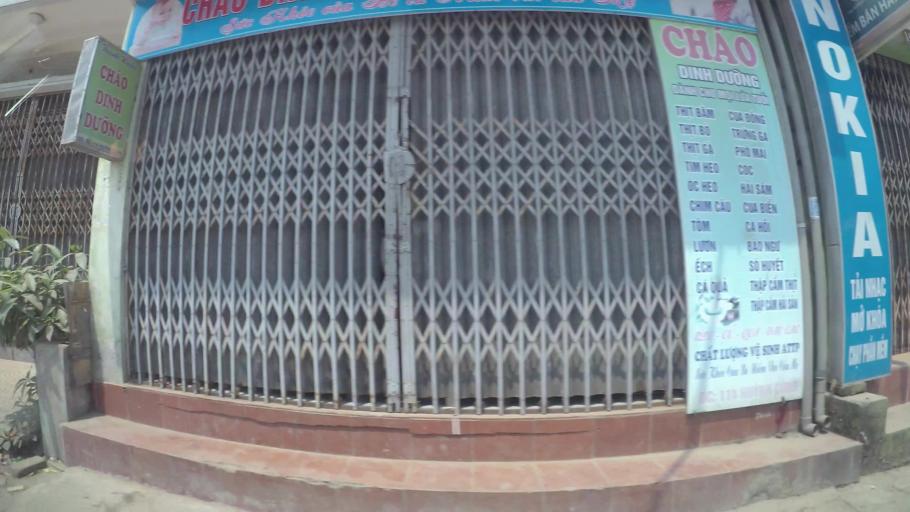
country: VN
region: Ha Noi
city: Van Dien
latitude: 20.9525
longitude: 105.8278
